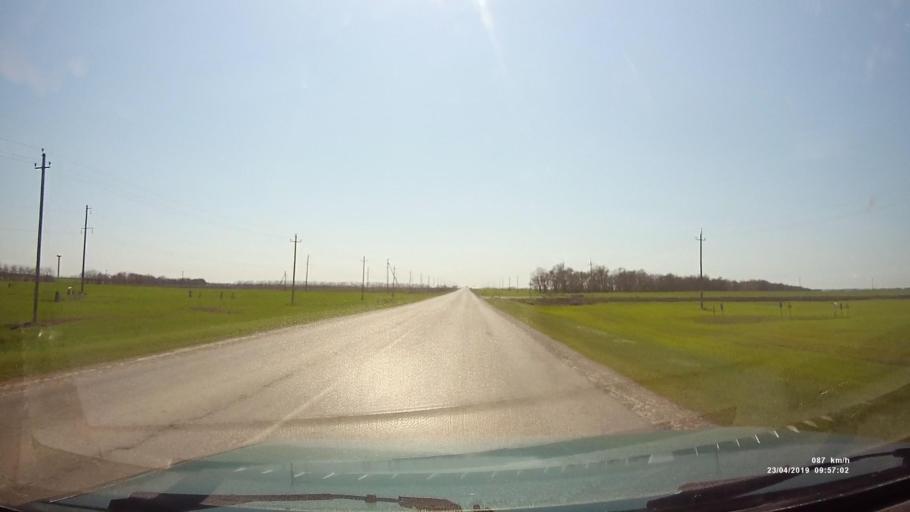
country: RU
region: Rostov
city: Orlovskiy
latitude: 46.7925
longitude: 42.0802
